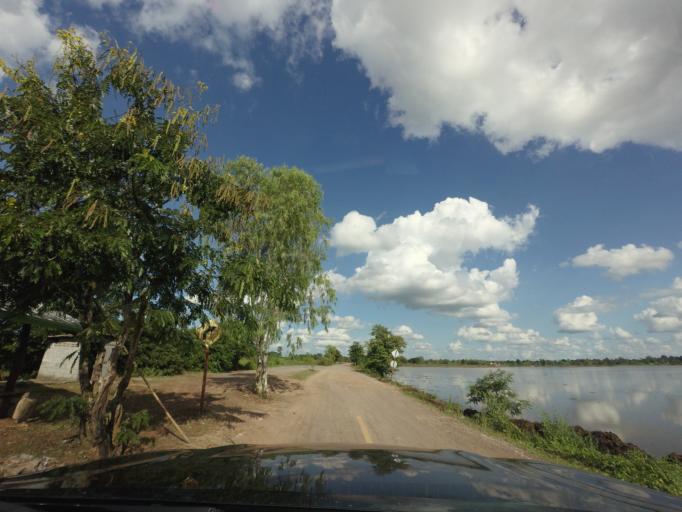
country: TH
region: Changwat Udon Thani
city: Ban Dung
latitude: 17.7504
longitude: 103.3597
